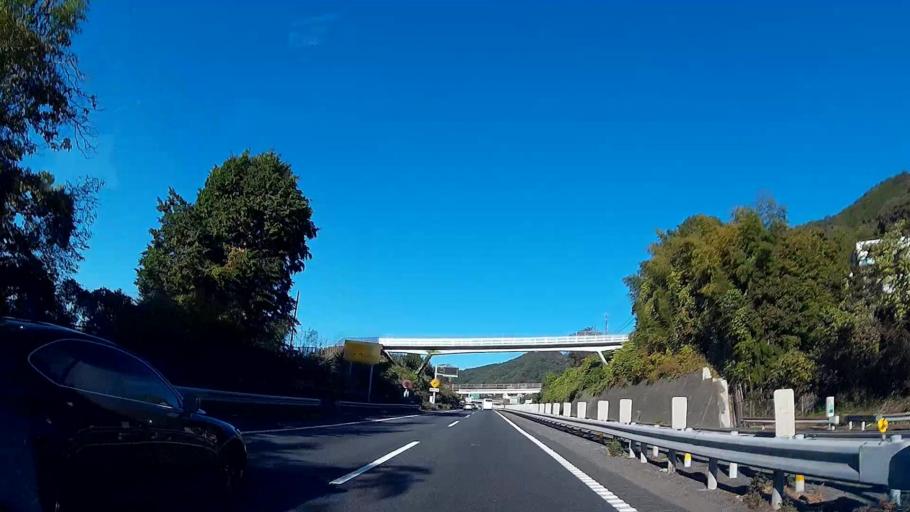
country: JP
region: Yamanashi
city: Uenohara
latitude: 35.6213
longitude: 139.1778
